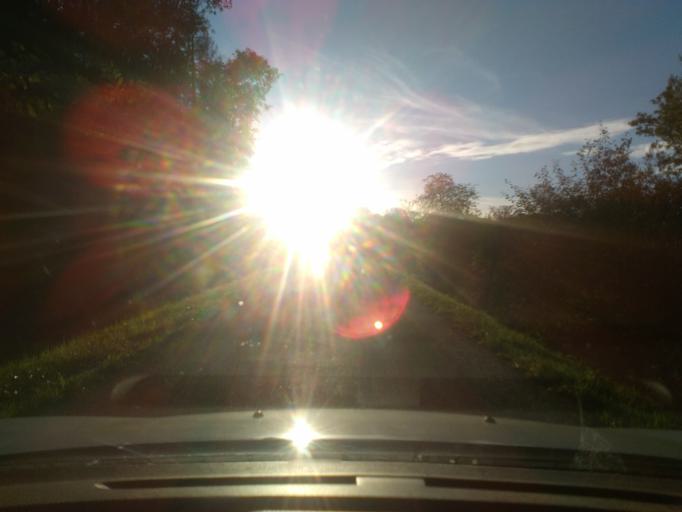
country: FR
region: Lorraine
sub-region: Departement des Vosges
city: Vincey
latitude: 48.3315
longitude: 6.3150
